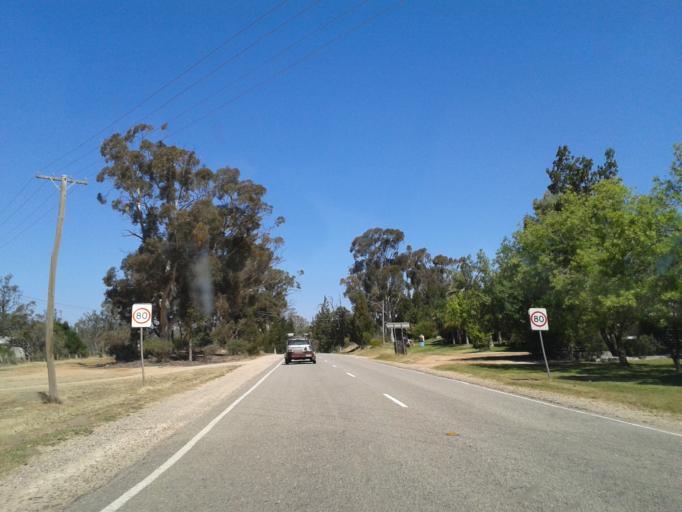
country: AU
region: Victoria
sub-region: Swan Hill
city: Swan Hill
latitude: -35.1055
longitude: 143.3463
